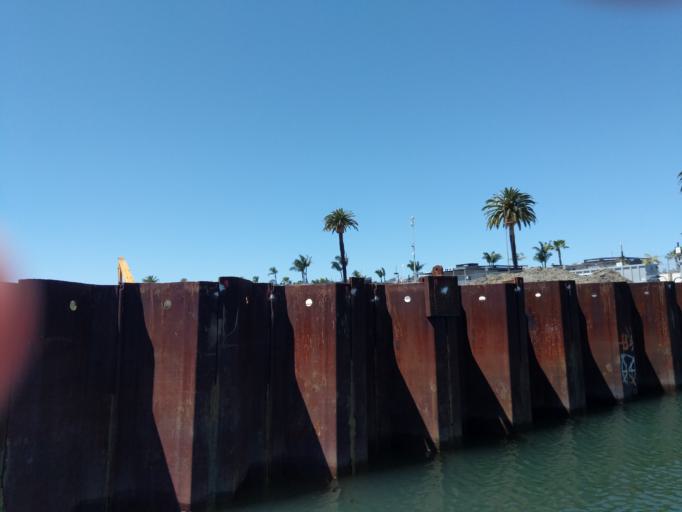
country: US
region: California
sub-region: San Diego County
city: Coronado
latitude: 32.7155
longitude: -117.2229
